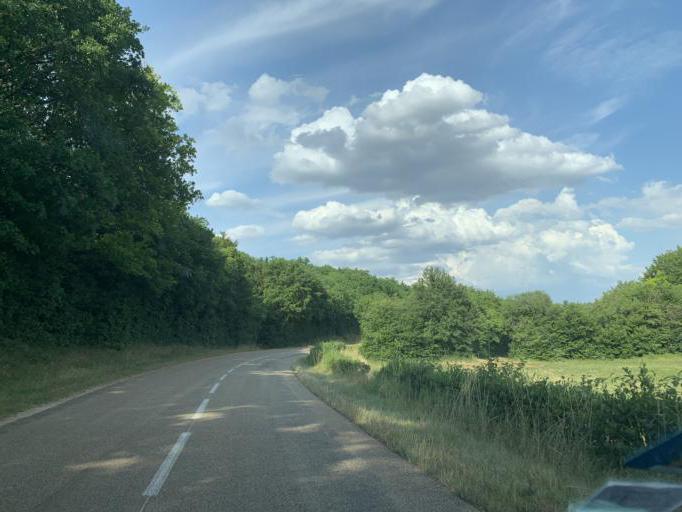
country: FR
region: Bourgogne
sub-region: Departement de l'Yonne
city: Fontenailles
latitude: 47.5321
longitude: 3.3959
